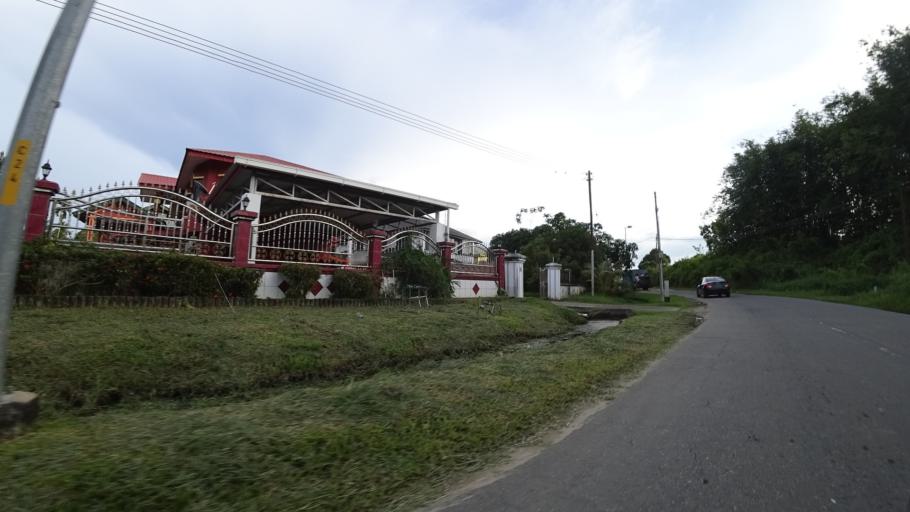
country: BN
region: Brunei and Muara
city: Bandar Seri Begawan
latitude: 4.8599
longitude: 114.8215
